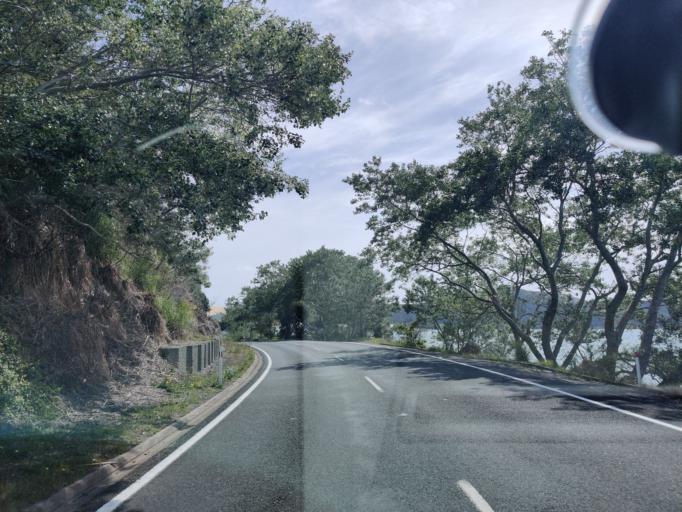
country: NZ
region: Northland
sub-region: Far North District
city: Ahipara
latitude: -35.5034
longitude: 173.3958
